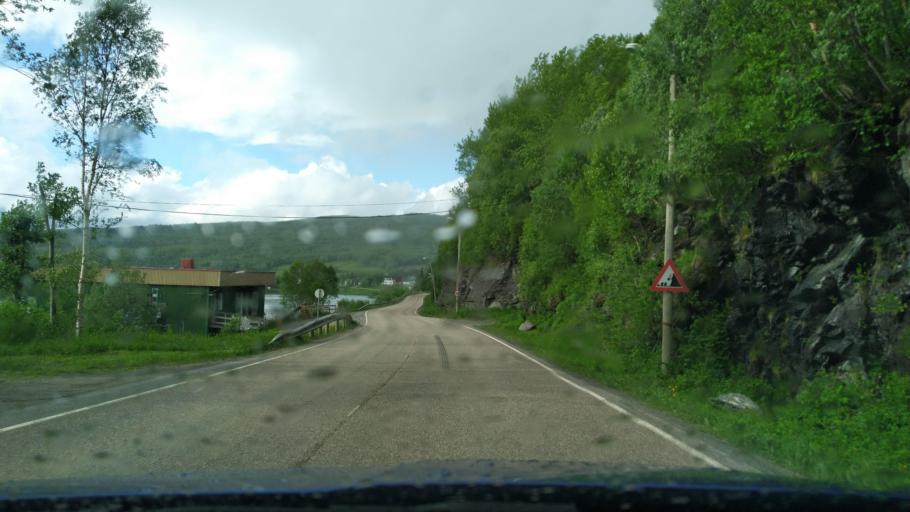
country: NO
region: Troms
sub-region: Sorreisa
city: Sorreisa
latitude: 69.1635
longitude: 18.1171
